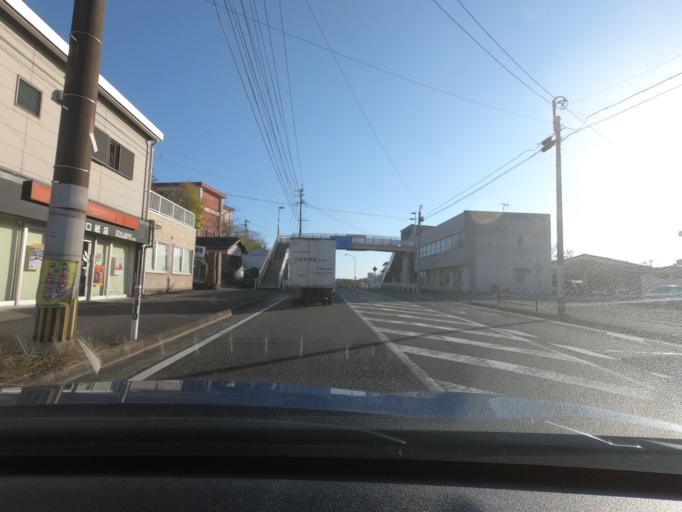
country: JP
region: Kagoshima
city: Akune
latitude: 32.0200
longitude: 130.1958
